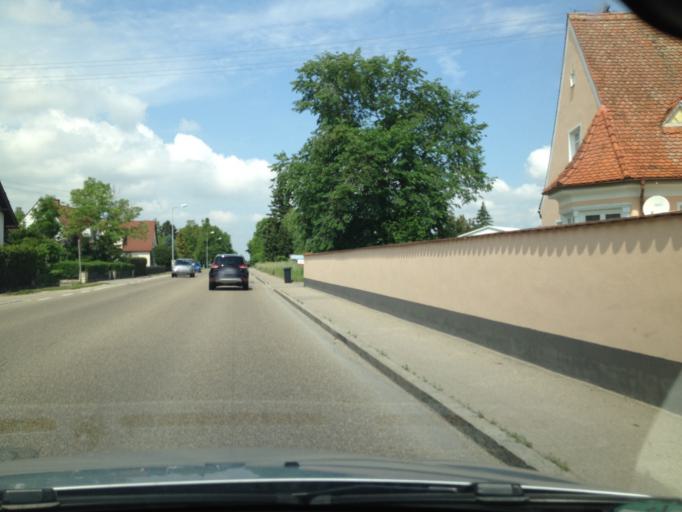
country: DE
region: Bavaria
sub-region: Swabia
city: Mottingen
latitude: 48.8072
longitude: 10.5957
